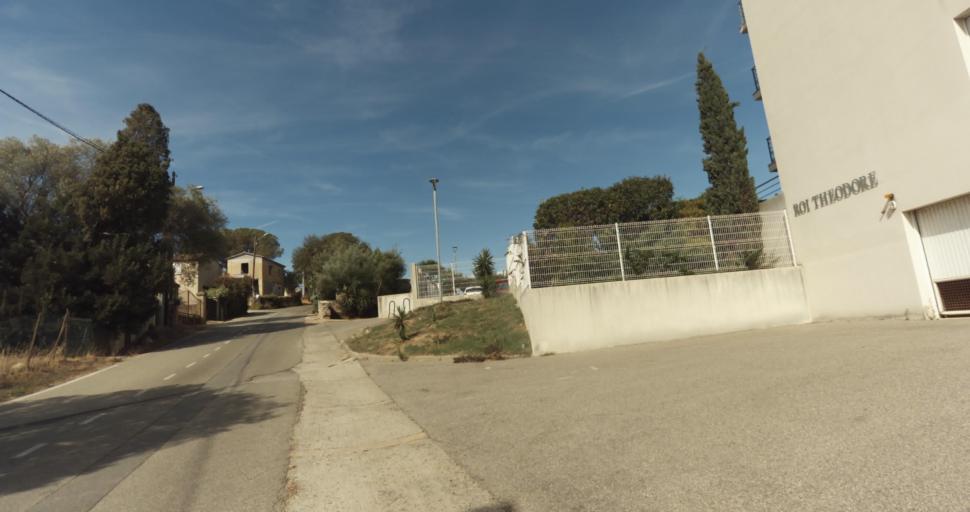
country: FR
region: Corsica
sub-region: Departement de la Corse-du-Sud
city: Ajaccio
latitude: 41.9389
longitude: 8.7352
